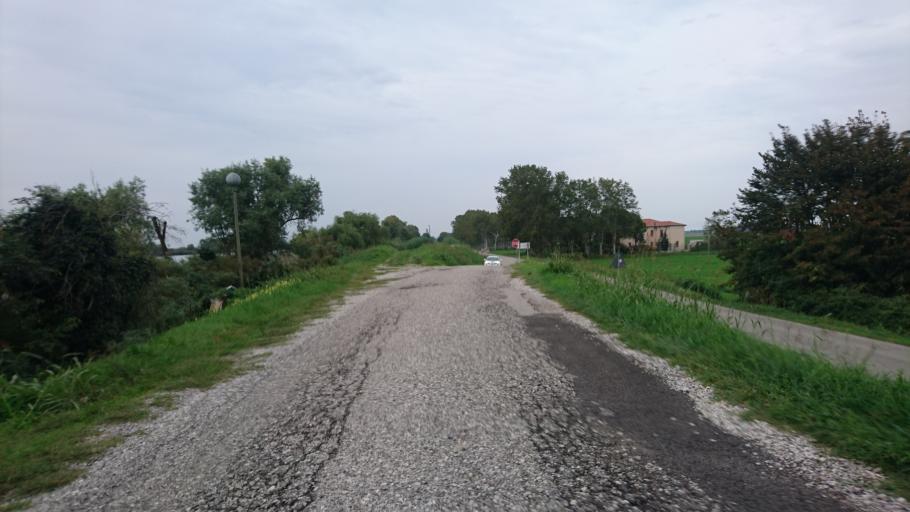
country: IT
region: Emilia-Romagna
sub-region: Provincia di Ferrara
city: Goro
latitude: 44.8405
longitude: 12.3755
